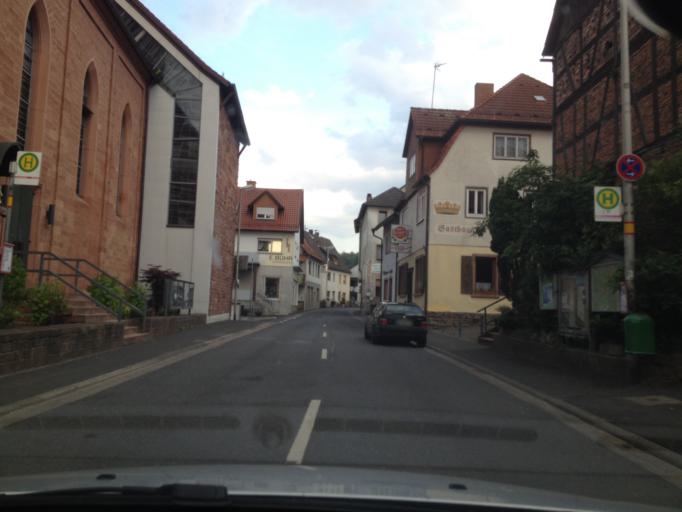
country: DE
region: Bavaria
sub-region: Regierungsbezirk Unterfranken
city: Weibersbrunn
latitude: 49.9307
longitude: 9.3677
